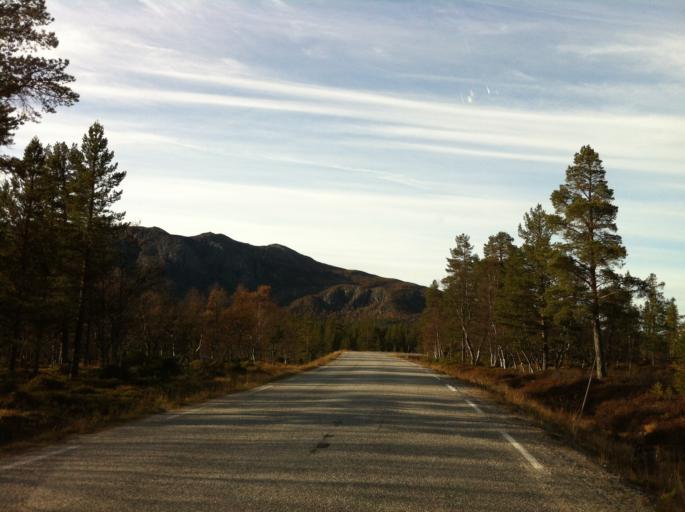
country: NO
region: Hedmark
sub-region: Engerdal
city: Engerdal
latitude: 62.0885
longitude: 12.0528
